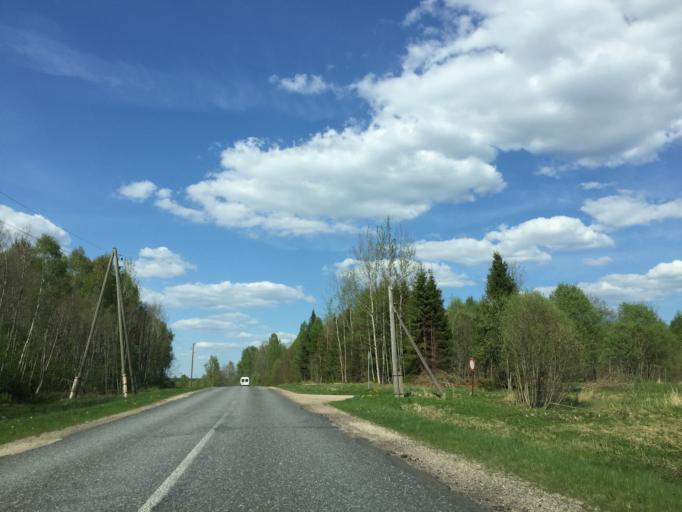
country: LV
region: Limbazu Rajons
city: Limbazi
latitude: 57.4416
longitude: 24.7226
